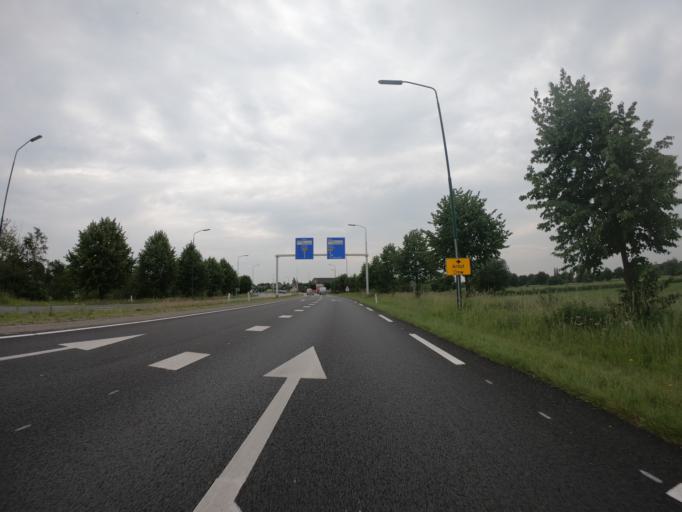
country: NL
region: North Brabant
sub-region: Gemeente Uden
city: Uden
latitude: 51.6481
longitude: 5.6081
